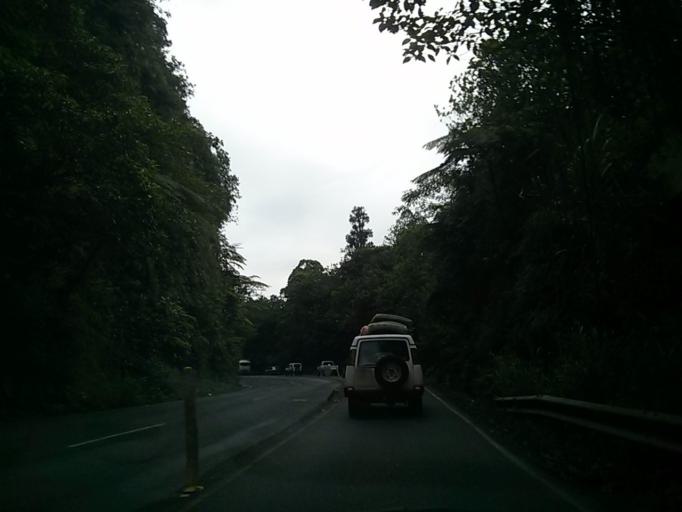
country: CR
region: San Jose
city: Dulce Nombre de Jesus
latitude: 10.1493
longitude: -83.9734
